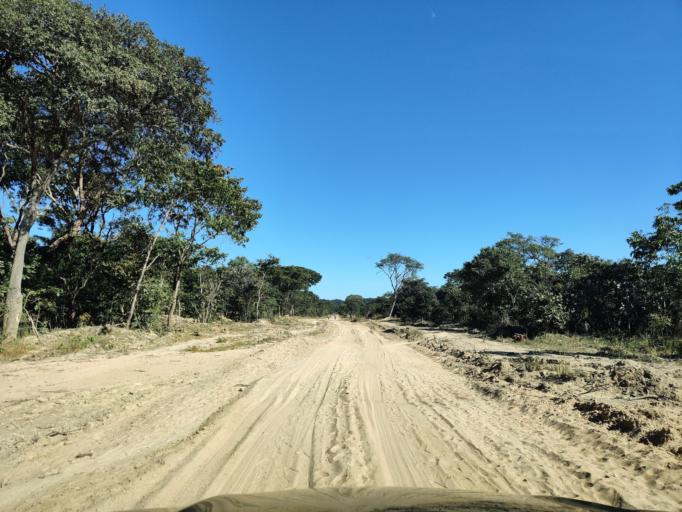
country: ZM
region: Central
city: Mkushi
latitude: -13.5133
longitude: 29.0123
